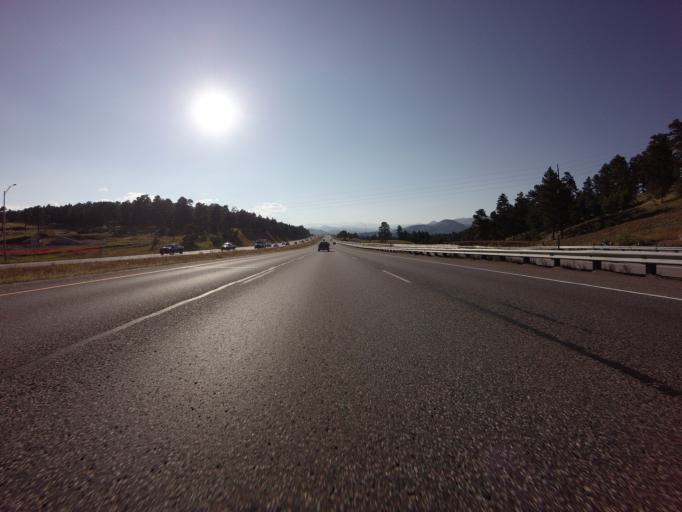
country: US
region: Colorado
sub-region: Jefferson County
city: Genesee
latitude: 39.7116
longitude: -105.2999
